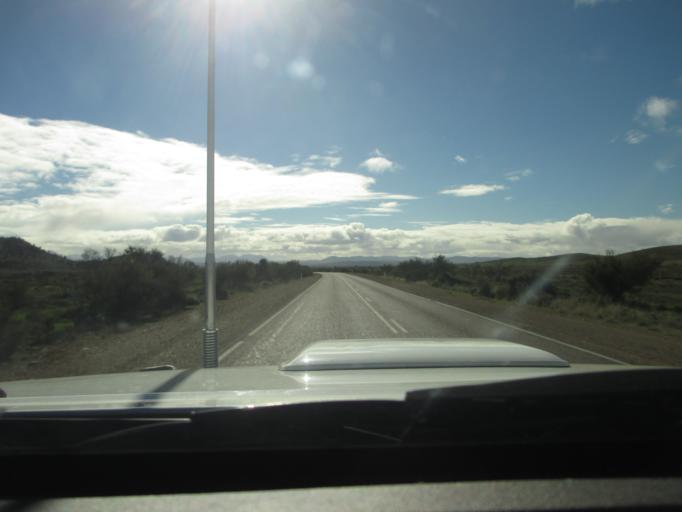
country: AU
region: South Australia
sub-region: Flinders Ranges
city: Quorn
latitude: -31.9260
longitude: 138.4213
